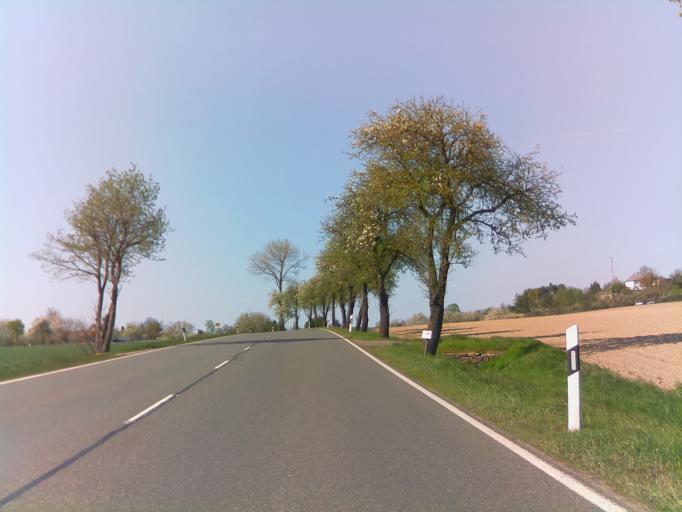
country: DE
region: Thuringia
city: Auma
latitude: 50.6909
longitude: 11.9078
